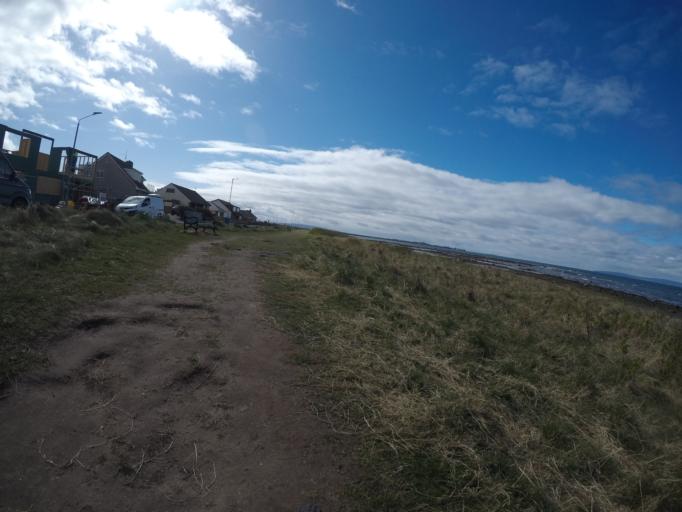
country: GB
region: Scotland
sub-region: South Ayrshire
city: Troon
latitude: 55.5677
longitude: -4.6578
